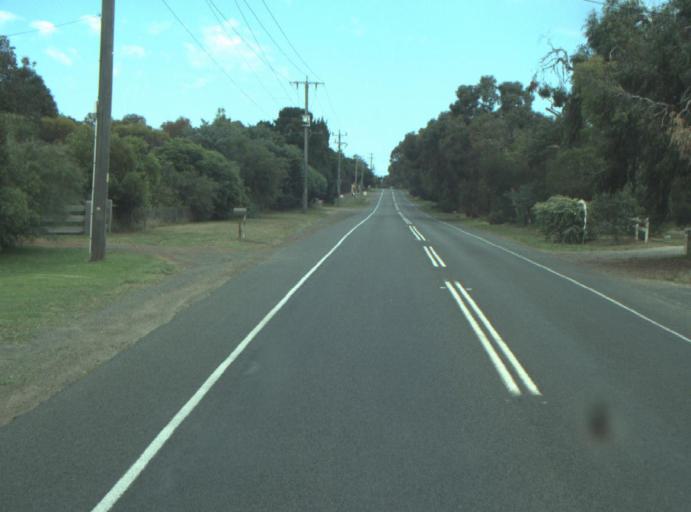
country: AU
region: Victoria
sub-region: Greater Geelong
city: Leopold
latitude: -38.2315
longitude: 144.5031
